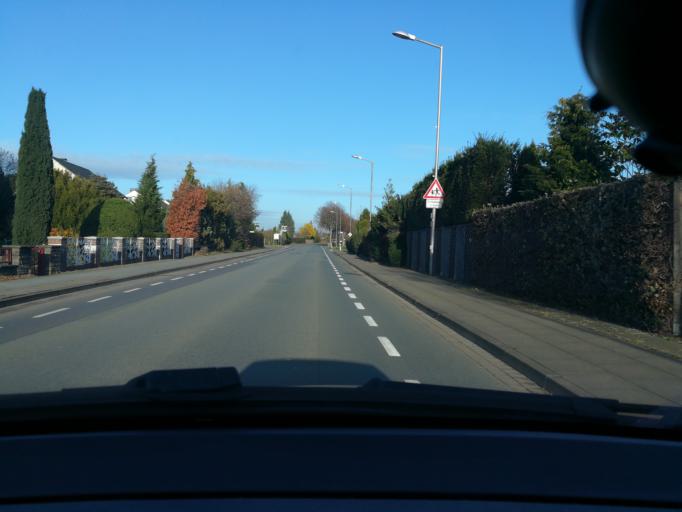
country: DE
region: North Rhine-Westphalia
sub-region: Regierungsbezirk Detmold
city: Minden
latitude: 52.3134
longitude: 8.9368
